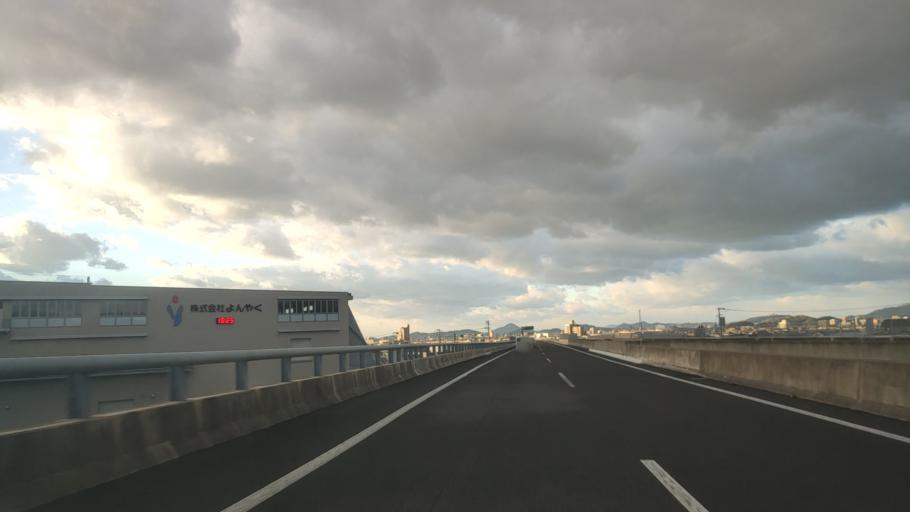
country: JP
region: Ehime
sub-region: Shikoku-chuo Shi
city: Matsuyama
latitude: 33.7901
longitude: 132.8050
